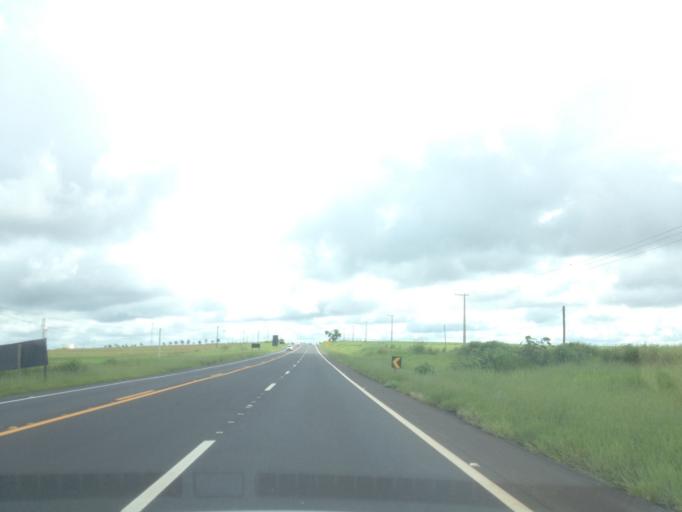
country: BR
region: Sao Paulo
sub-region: Marilia
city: Marilia
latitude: -22.2633
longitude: -49.9951
